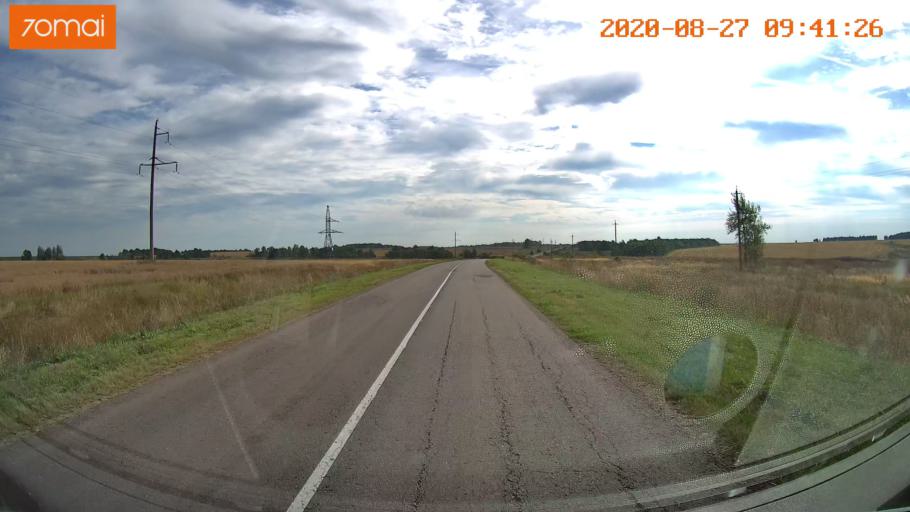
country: RU
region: Tula
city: Kurkino
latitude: 53.3771
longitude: 38.4203
